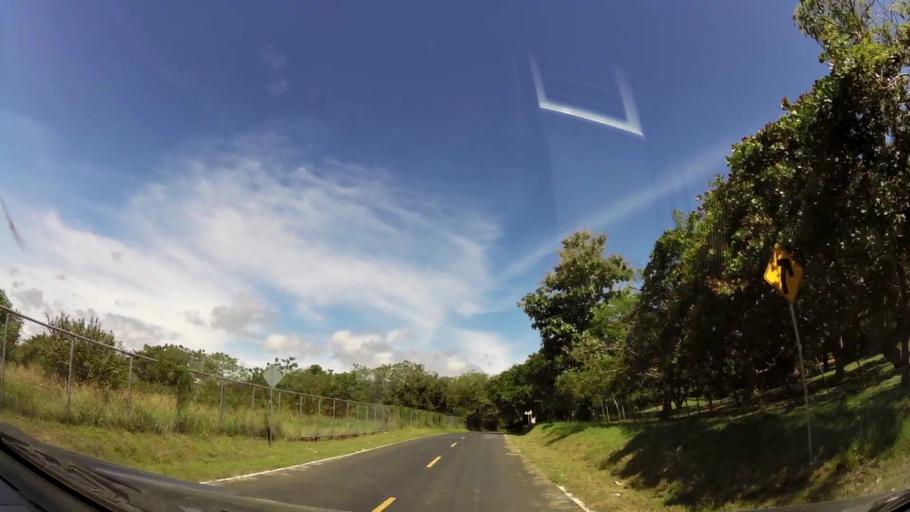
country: PA
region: Panama
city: Nueva Gorgona
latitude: 8.5593
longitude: -79.8674
